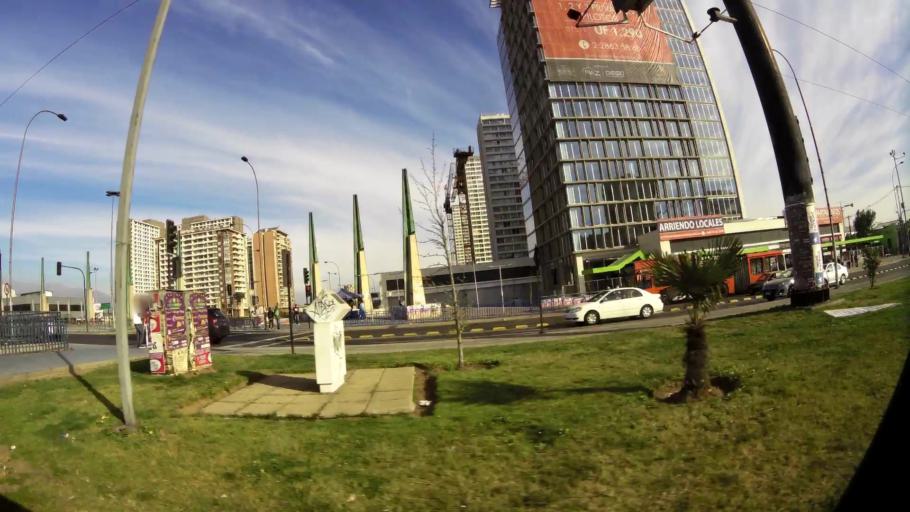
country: CL
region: Santiago Metropolitan
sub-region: Provincia de Santiago
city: Lo Prado
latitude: -33.4539
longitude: -70.6914
